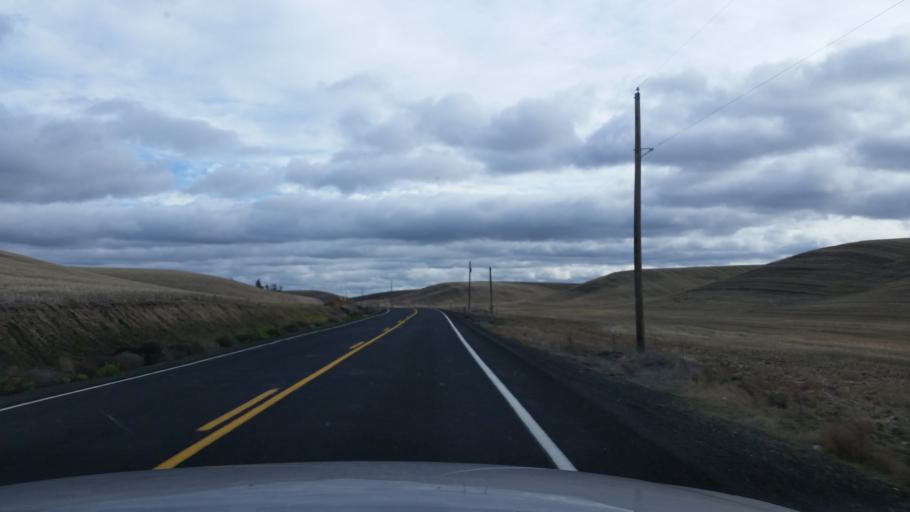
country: US
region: Washington
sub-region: Lincoln County
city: Davenport
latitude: 47.3528
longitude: -118.0312
